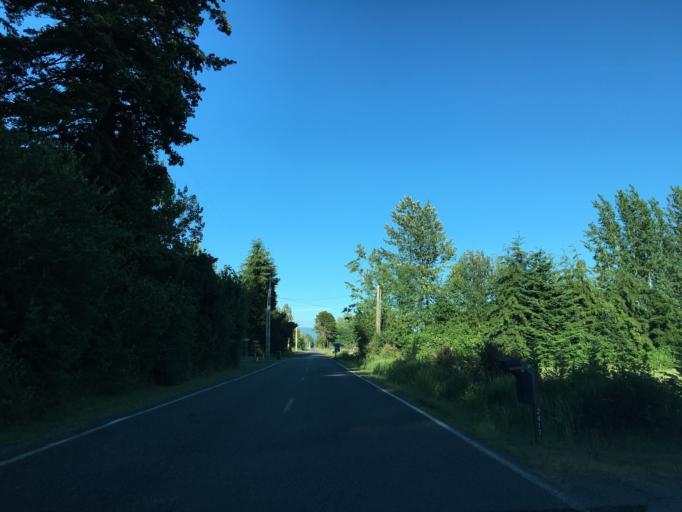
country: US
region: Washington
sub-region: Whatcom County
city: Ferndale
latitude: 48.9062
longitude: -122.6119
